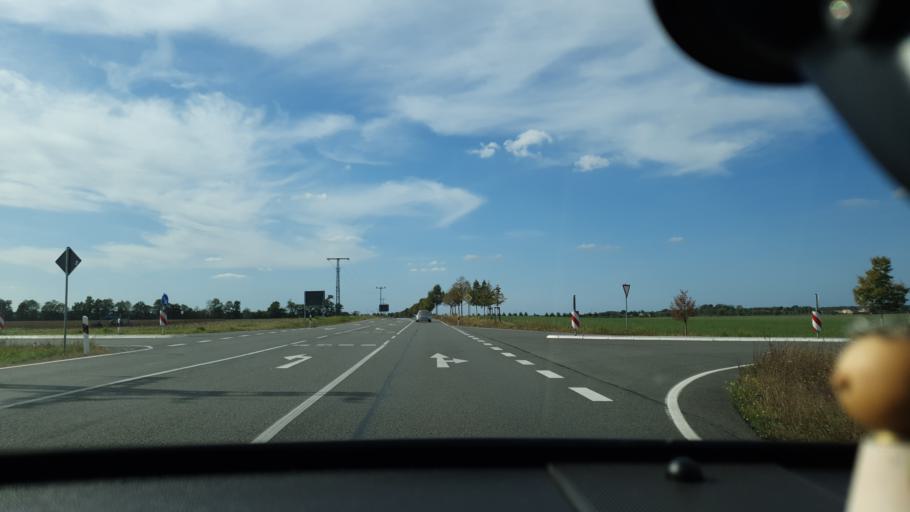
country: DE
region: Saxony
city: Jesewitz
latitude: 51.4567
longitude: 12.5461
